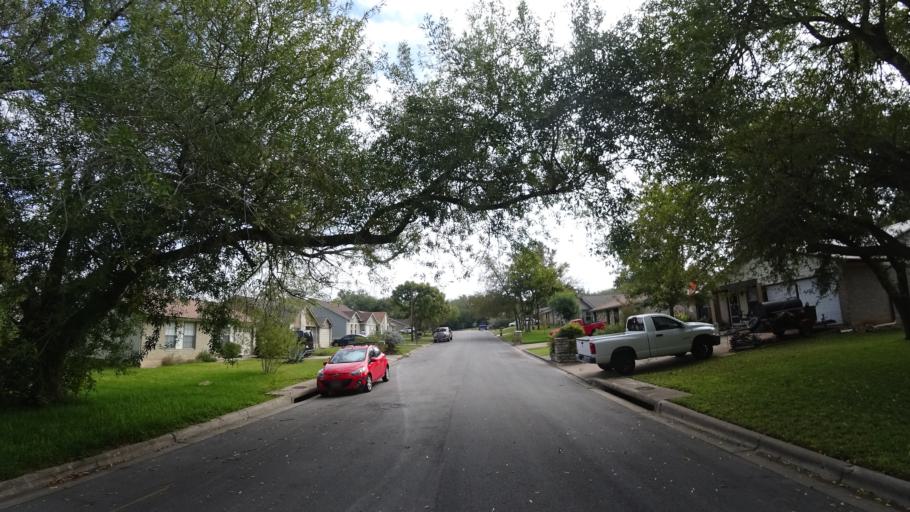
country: US
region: Texas
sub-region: Travis County
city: Shady Hollow
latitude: 30.1985
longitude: -97.8342
